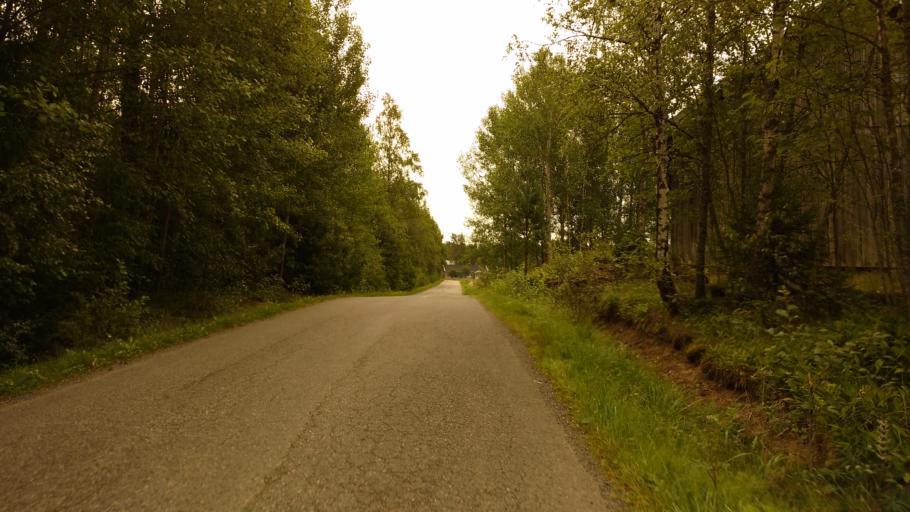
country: FI
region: Varsinais-Suomi
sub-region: Turku
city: Piikkioe
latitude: 60.4380
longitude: 22.4434
